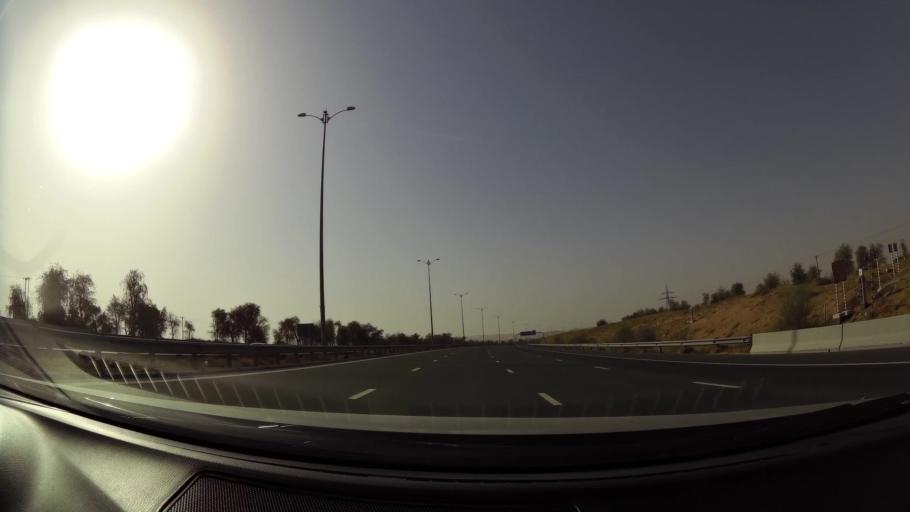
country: OM
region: Al Buraimi
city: Al Buraymi
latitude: 24.6536
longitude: 55.6997
